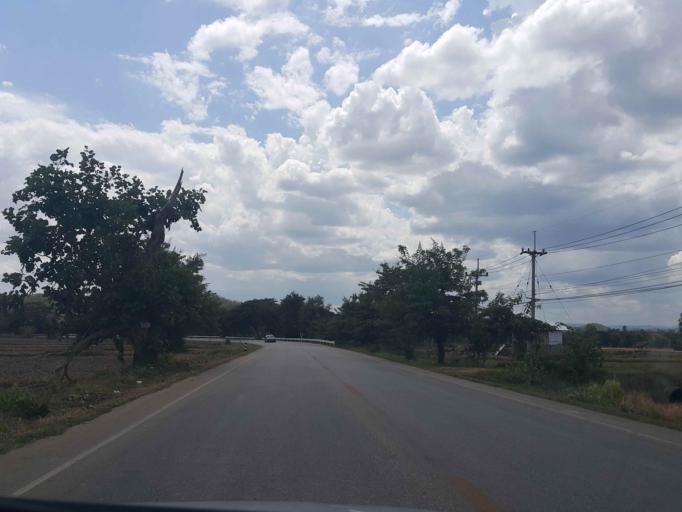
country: TH
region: Sukhothai
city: Thung Saliam
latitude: 17.3431
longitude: 99.5997
